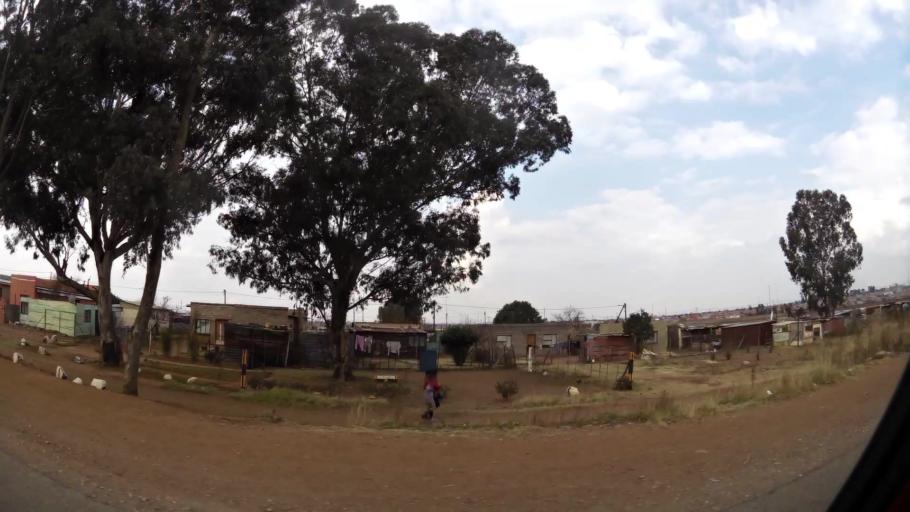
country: ZA
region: Gauteng
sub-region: Sedibeng District Municipality
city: Vanderbijlpark
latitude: -26.6684
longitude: 27.8630
